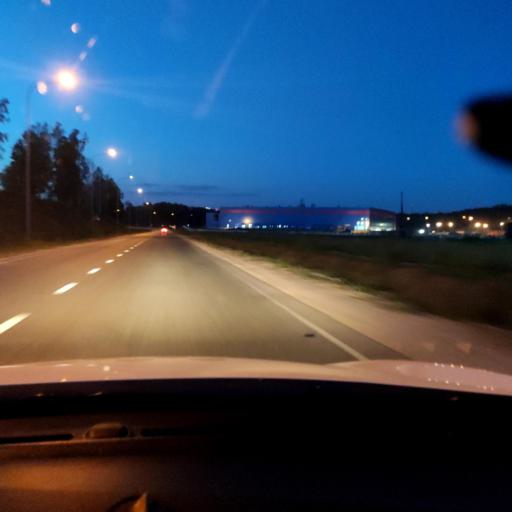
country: RU
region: Tatarstan
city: Osinovo
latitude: 55.8533
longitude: 48.8417
